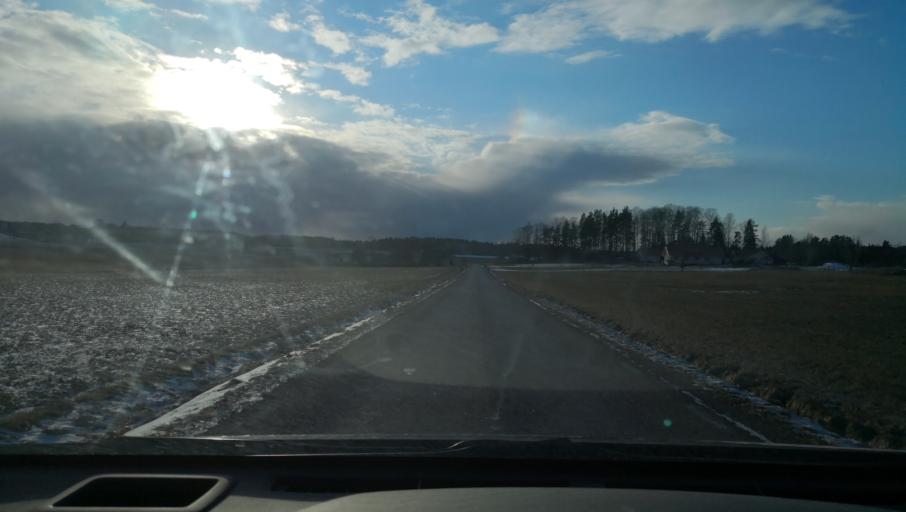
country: SE
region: Uppsala
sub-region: Enkopings Kommun
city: Irsta
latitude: 59.6605
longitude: 16.8158
